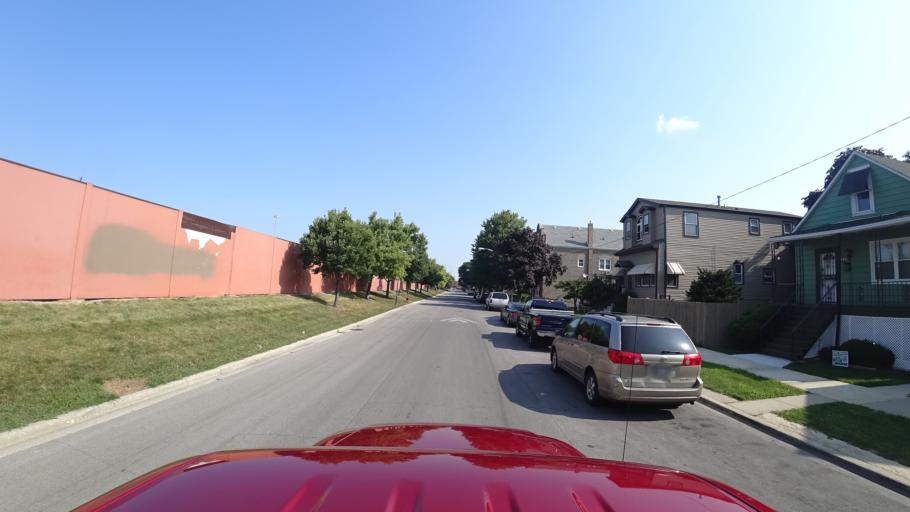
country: US
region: Illinois
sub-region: Cook County
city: Cicero
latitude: 41.8121
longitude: -87.7126
